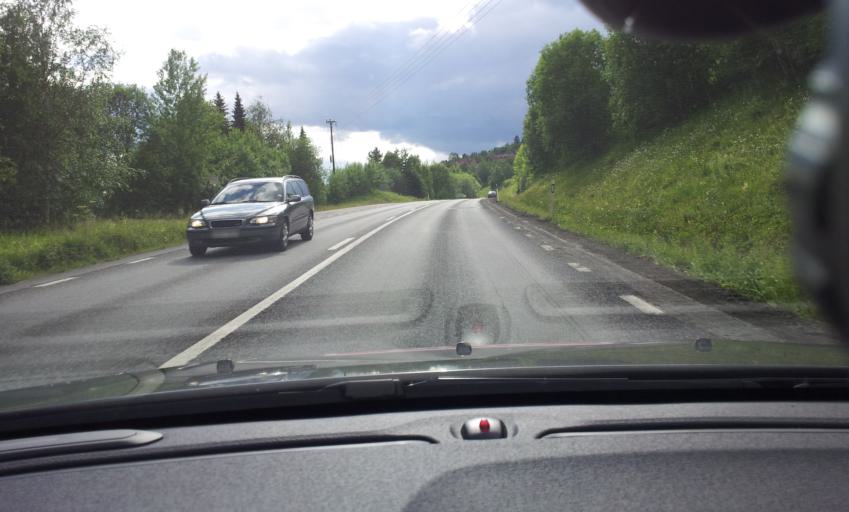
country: SE
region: Jaemtland
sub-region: Are Kommun
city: Jarpen
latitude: 63.3216
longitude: 13.3633
